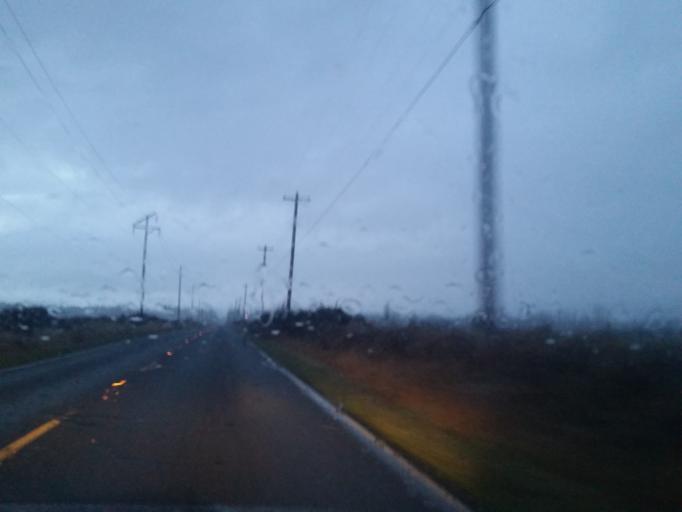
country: US
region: Washington
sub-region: Snohomish County
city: Everett
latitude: 47.9555
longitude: -122.1738
